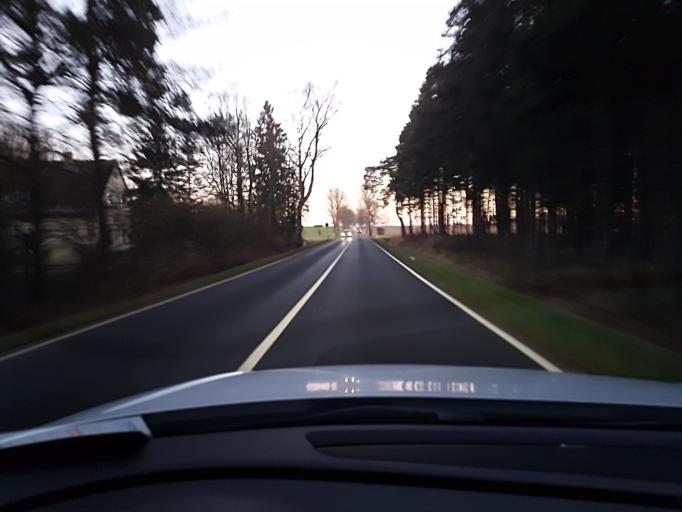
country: DE
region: Mecklenburg-Vorpommern
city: Gingst
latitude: 54.5021
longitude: 13.2786
